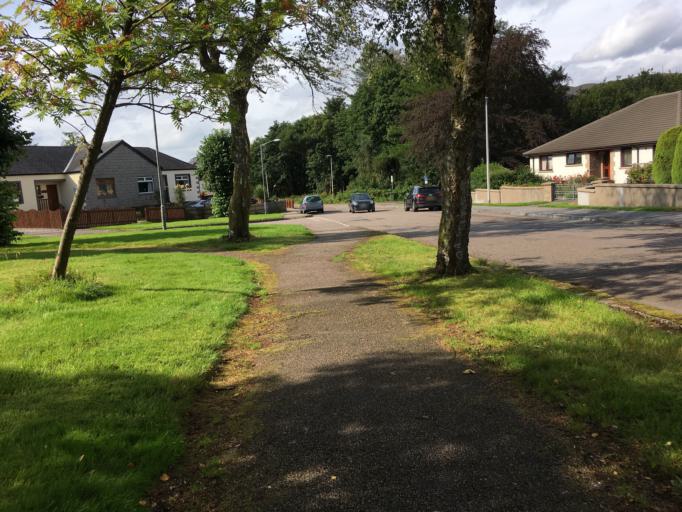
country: GB
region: Scotland
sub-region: Highland
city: Fort William
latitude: 56.8252
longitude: -5.0983
